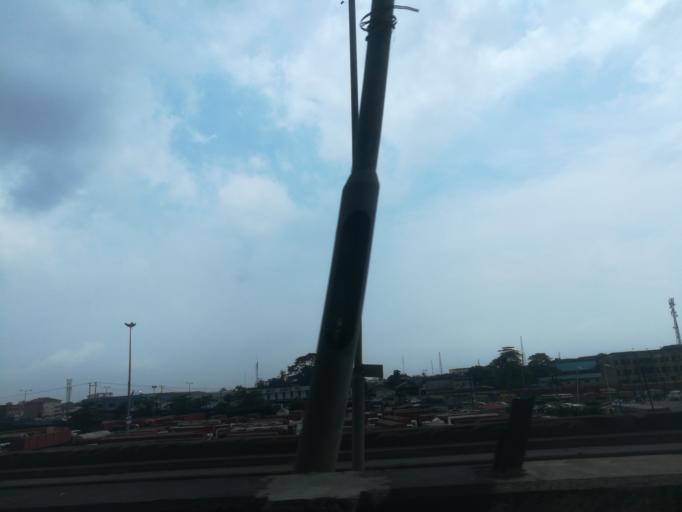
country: NG
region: Lagos
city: Ebute Metta
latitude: 6.4812
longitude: 3.3679
